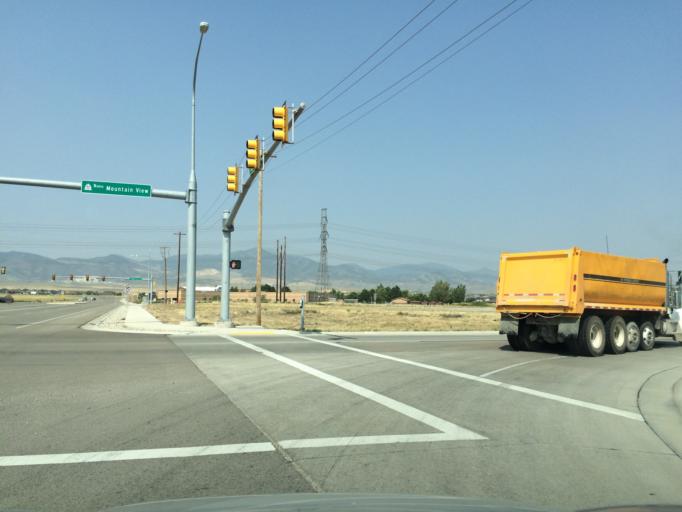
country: US
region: Utah
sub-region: Salt Lake County
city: Oquirrh
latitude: 40.5879
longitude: -112.0276
